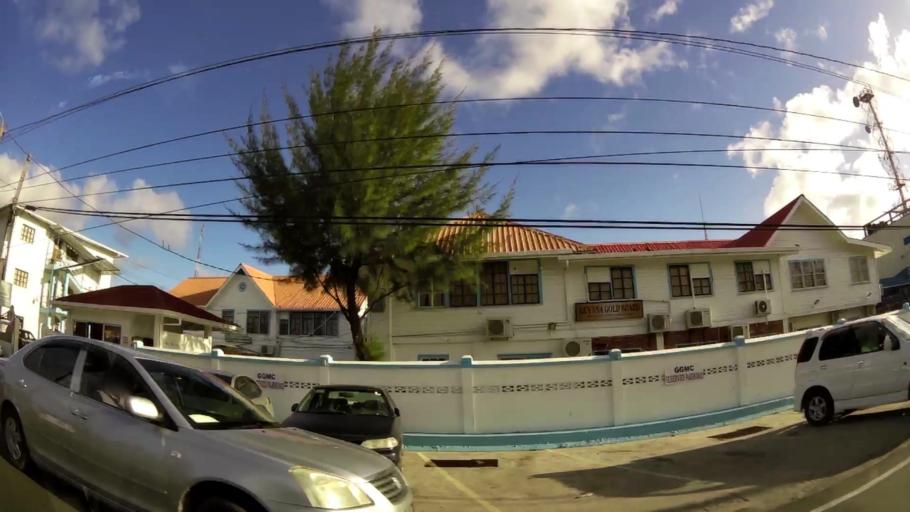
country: GY
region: Demerara-Mahaica
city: Georgetown
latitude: 6.8054
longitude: -58.1526
